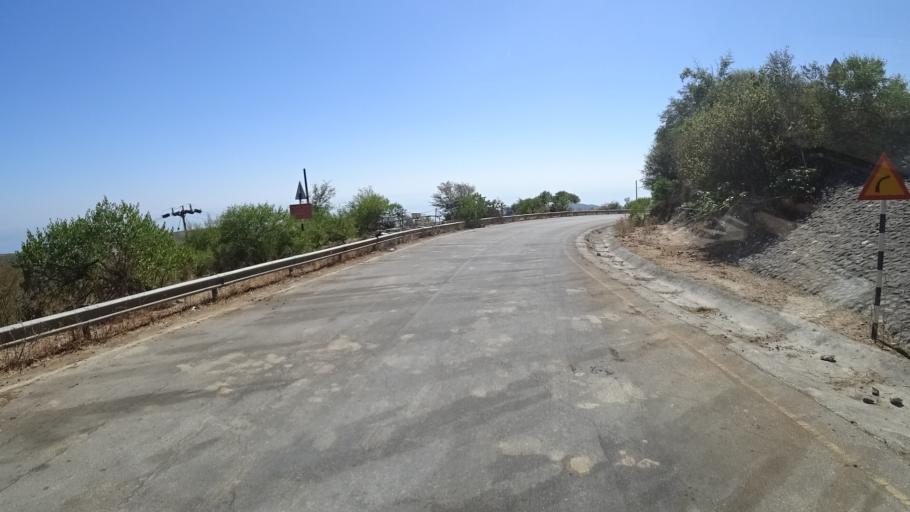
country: YE
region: Al Mahrah
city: Hawf
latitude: 16.7643
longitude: 53.3395
